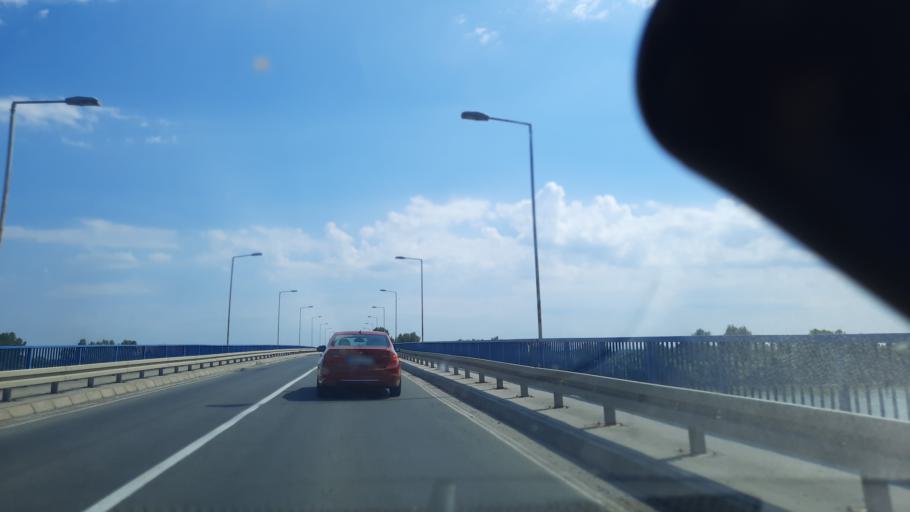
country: RS
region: Autonomna Pokrajina Vojvodina
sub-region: Sremski Okrug
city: Sremska Mitrovica
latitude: 44.9610
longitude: 19.6311
